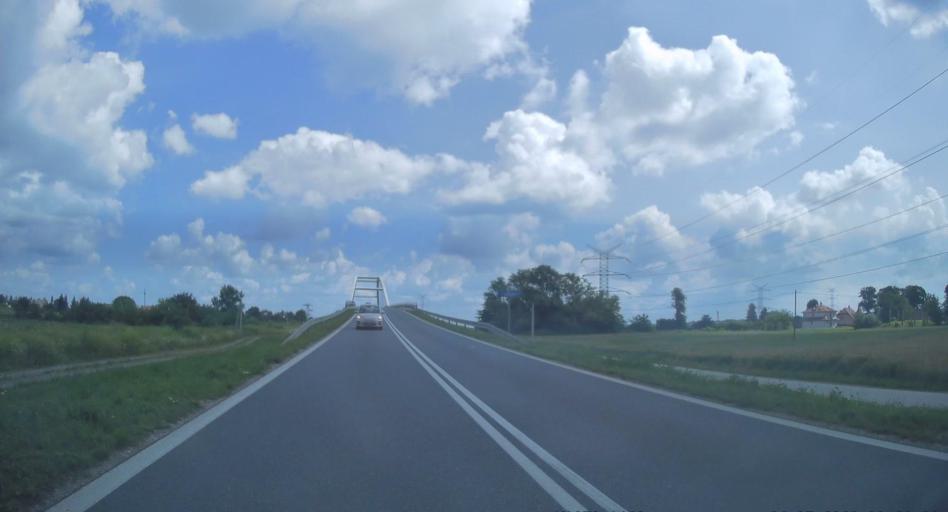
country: PL
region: Lesser Poland Voivodeship
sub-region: Powiat tarnowski
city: Wojnicz
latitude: 49.9494
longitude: 20.8487
